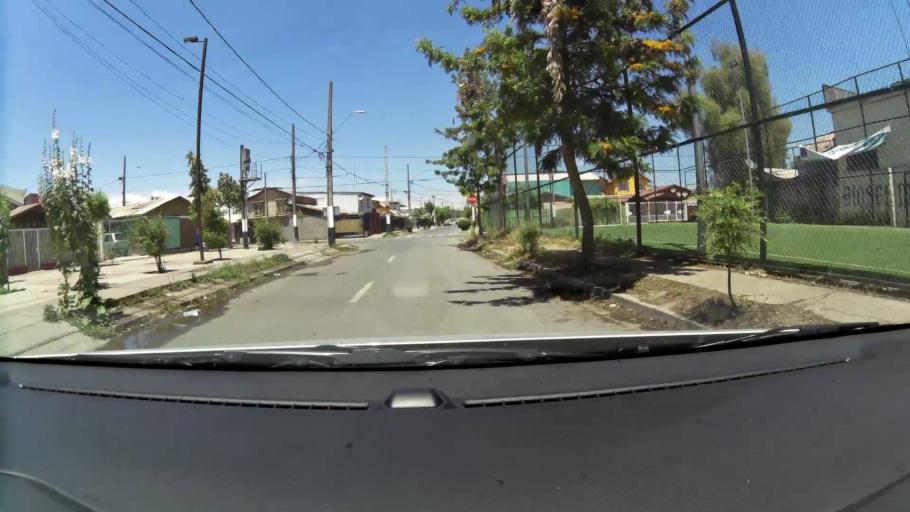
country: CL
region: Santiago Metropolitan
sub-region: Provincia de Santiago
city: La Pintana
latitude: -33.5621
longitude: -70.6429
